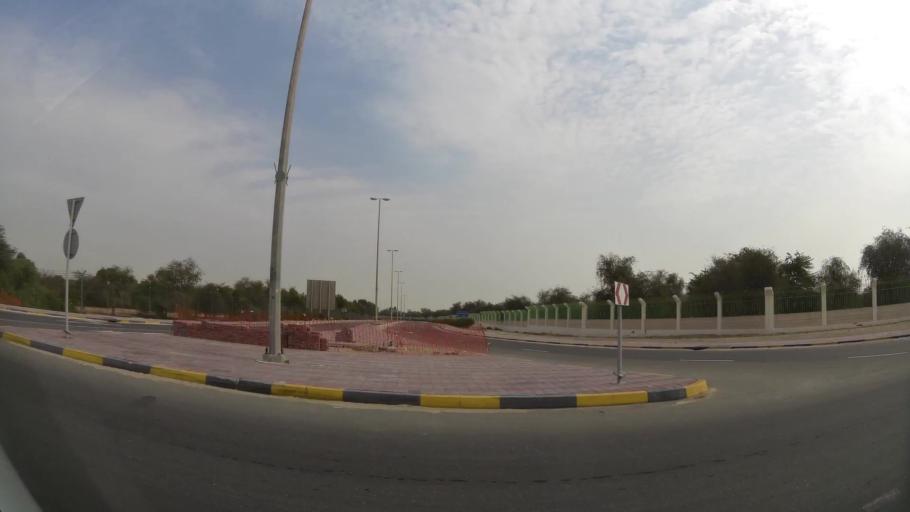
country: AE
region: Abu Dhabi
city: Abu Dhabi
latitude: 24.6885
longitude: 54.7704
